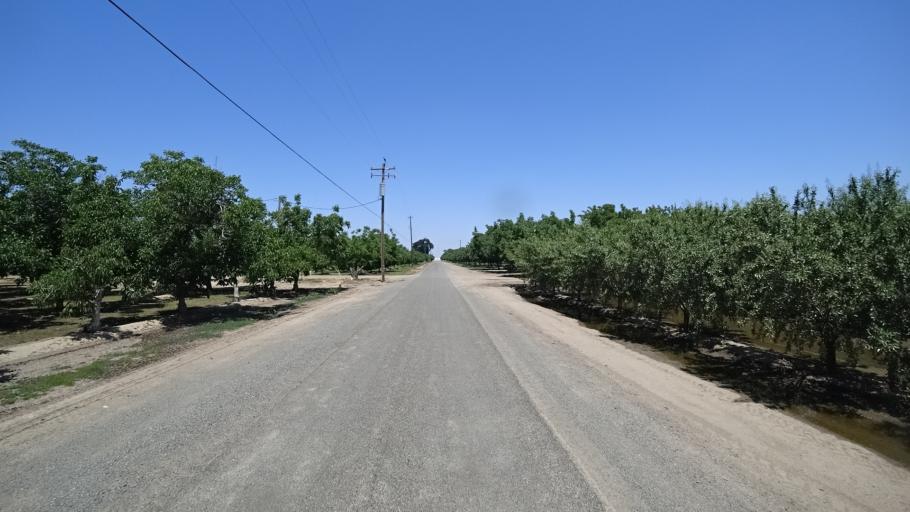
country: US
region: California
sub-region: Fresno County
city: Laton
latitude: 36.3963
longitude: -119.7368
